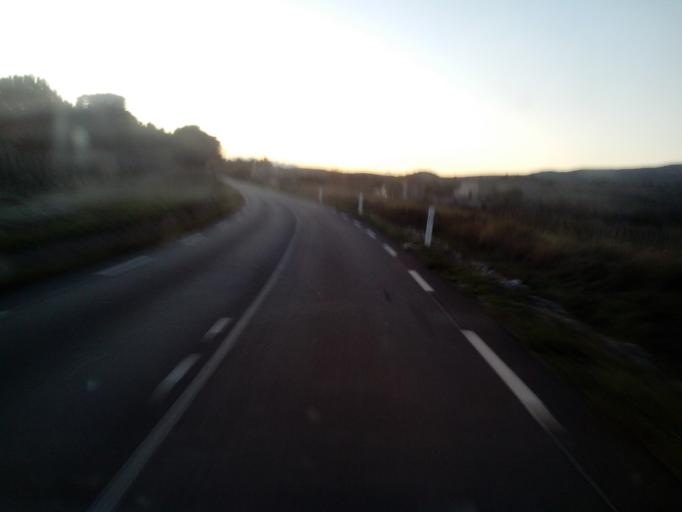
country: FR
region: Languedoc-Roussillon
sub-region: Departement des Pyrenees-Orientales
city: Baixas
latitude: 42.7822
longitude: 2.7985
